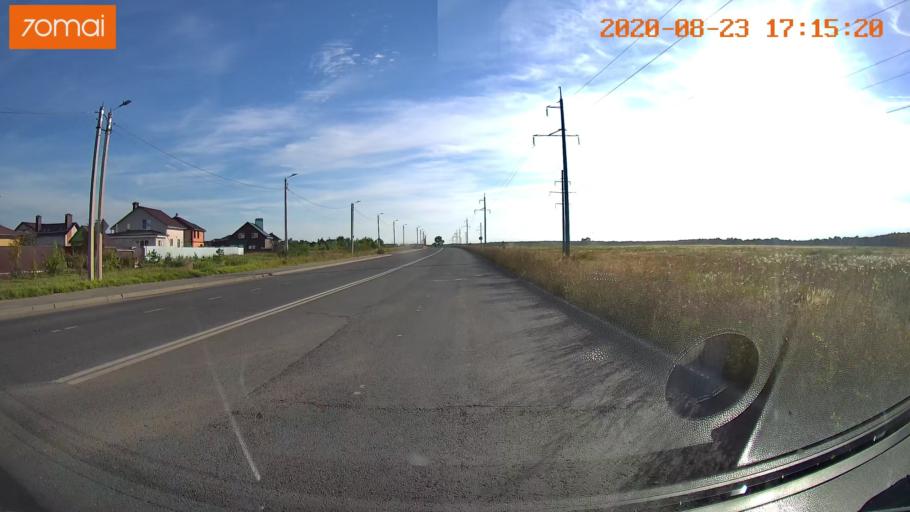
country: RU
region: Ivanovo
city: Novo-Talitsy
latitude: 57.0458
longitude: 40.9133
